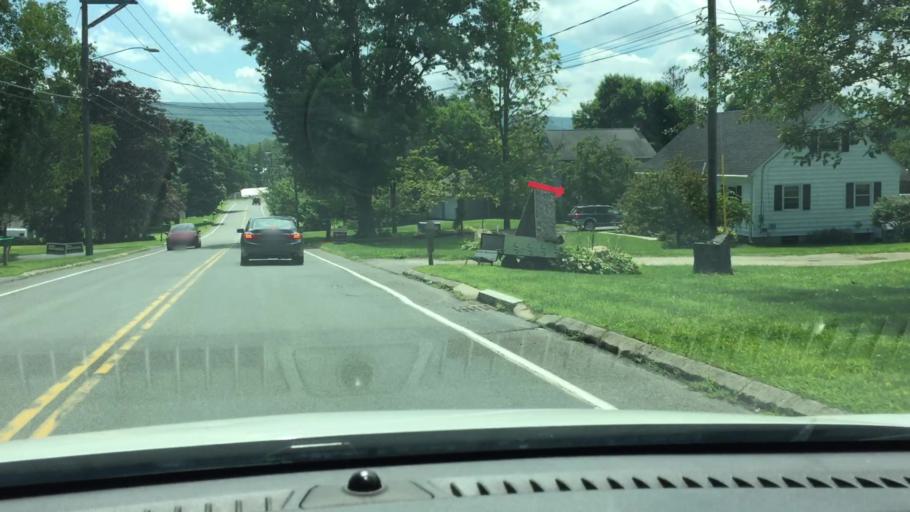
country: US
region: Massachusetts
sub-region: Berkshire County
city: Pittsfield
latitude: 42.4726
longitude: -73.2144
